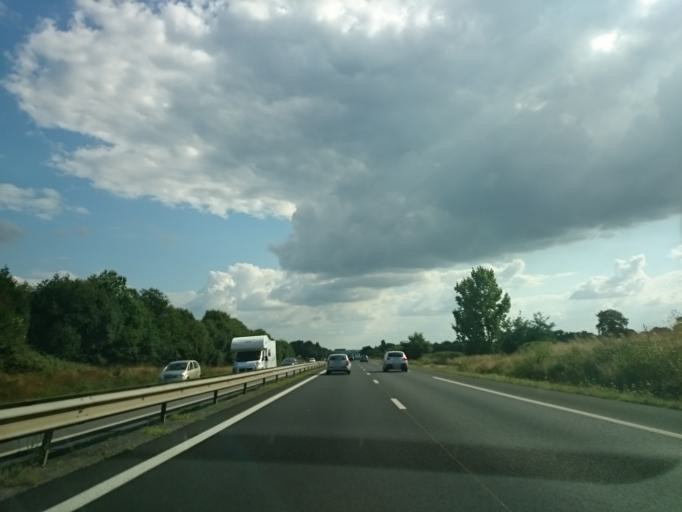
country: FR
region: Brittany
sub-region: Departement d'Ille-et-Vilaine
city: Chatillon-sur-Seiche
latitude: 48.0614
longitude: -1.6789
